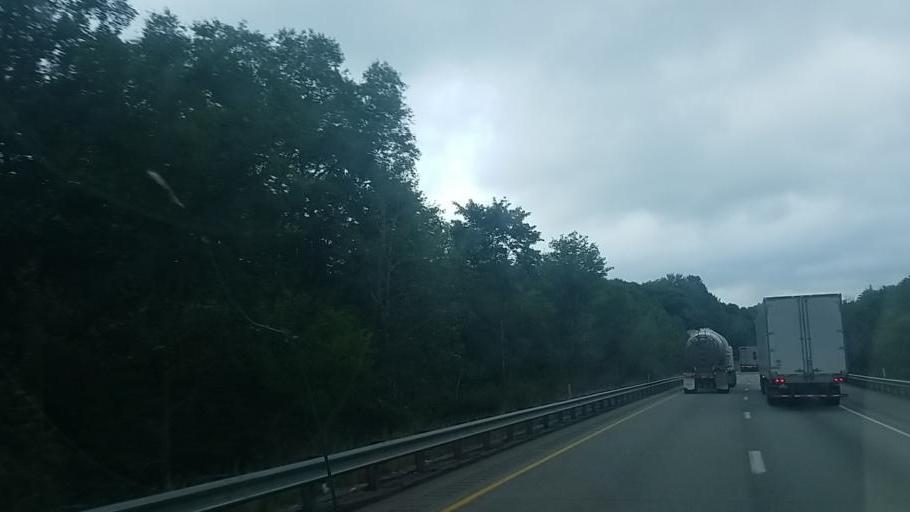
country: US
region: Pennsylvania
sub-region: Jefferson County
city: Falls Creek
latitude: 41.1570
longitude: -78.8322
